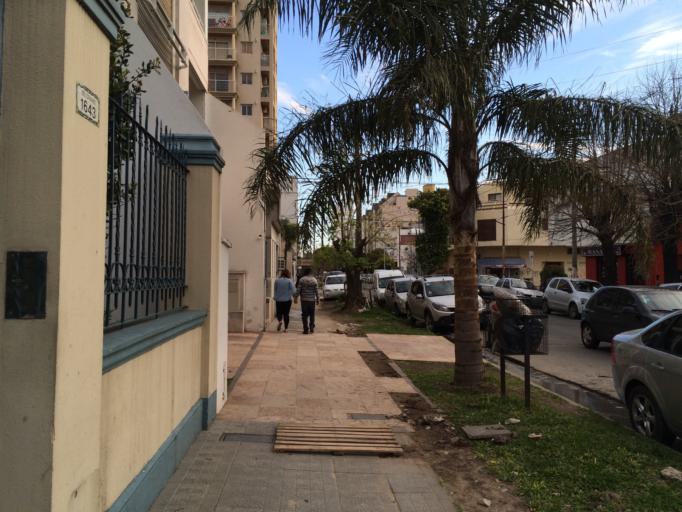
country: AR
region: Buenos Aires
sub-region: Partido de Lomas de Zamora
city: Lomas de Zamora
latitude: -34.7418
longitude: -58.3914
